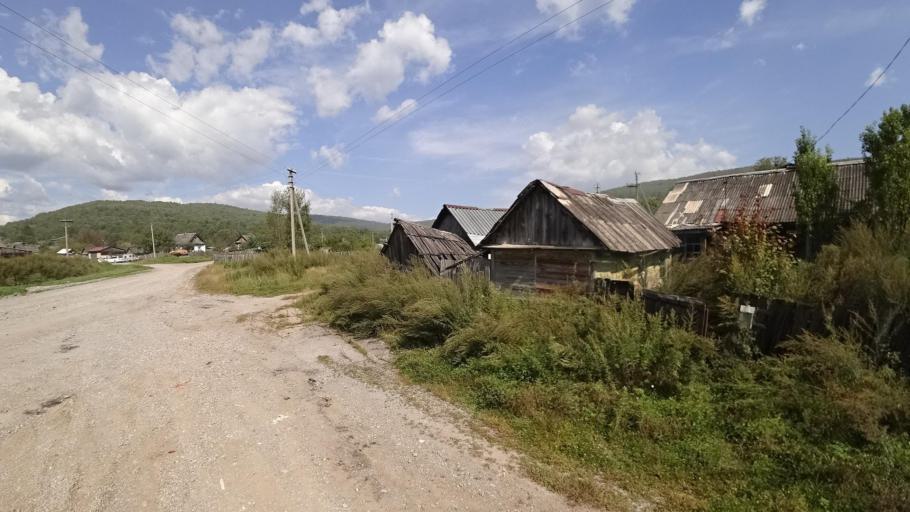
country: RU
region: Jewish Autonomous Oblast
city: Londoko
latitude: 49.0259
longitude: 131.9323
